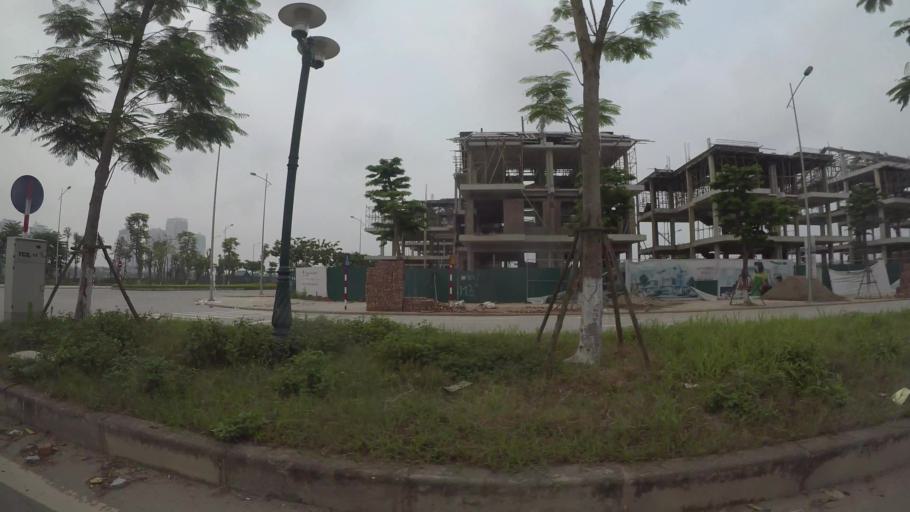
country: VN
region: Ha Noi
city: Ha Dong
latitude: 20.9836
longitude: 105.7561
